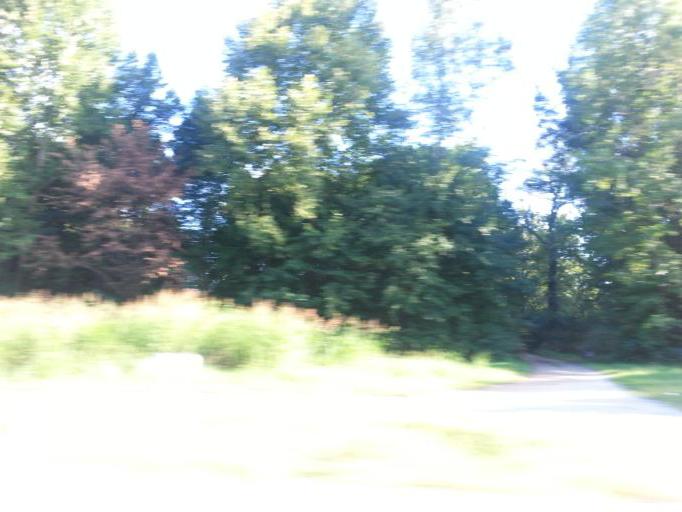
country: US
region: Alabama
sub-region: Lauderdale County
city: Killen
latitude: 34.8595
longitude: -87.5256
